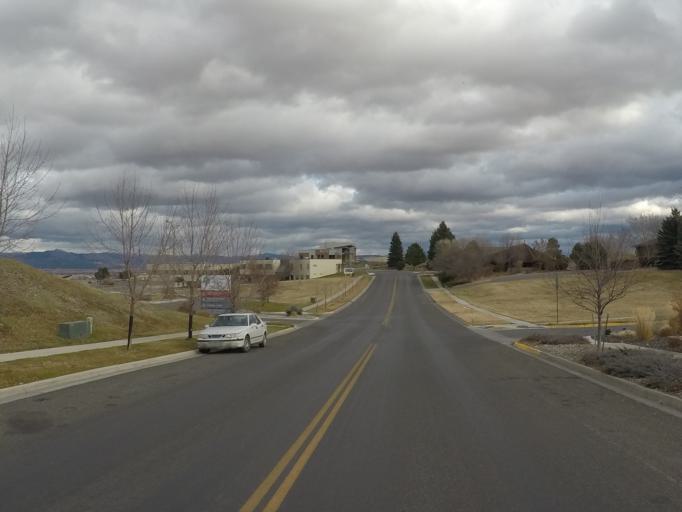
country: US
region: Montana
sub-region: Lewis and Clark County
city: Helena
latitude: 46.5814
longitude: -111.9963
